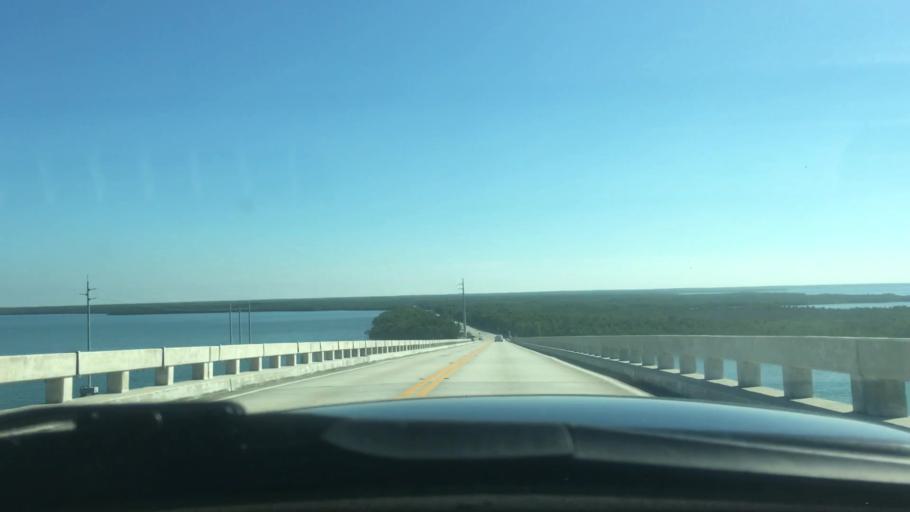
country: US
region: Florida
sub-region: Monroe County
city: North Key Largo
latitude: 25.2869
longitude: -80.3677
